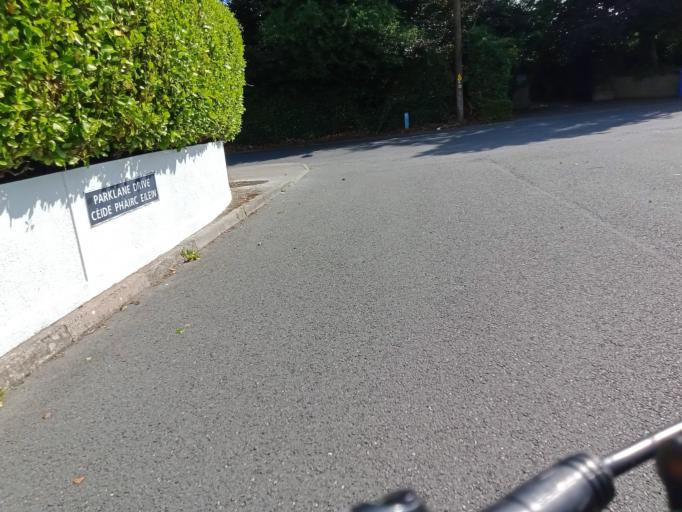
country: IE
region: Munster
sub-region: Waterford
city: Dungarvan
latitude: 52.0925
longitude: -7.6044
